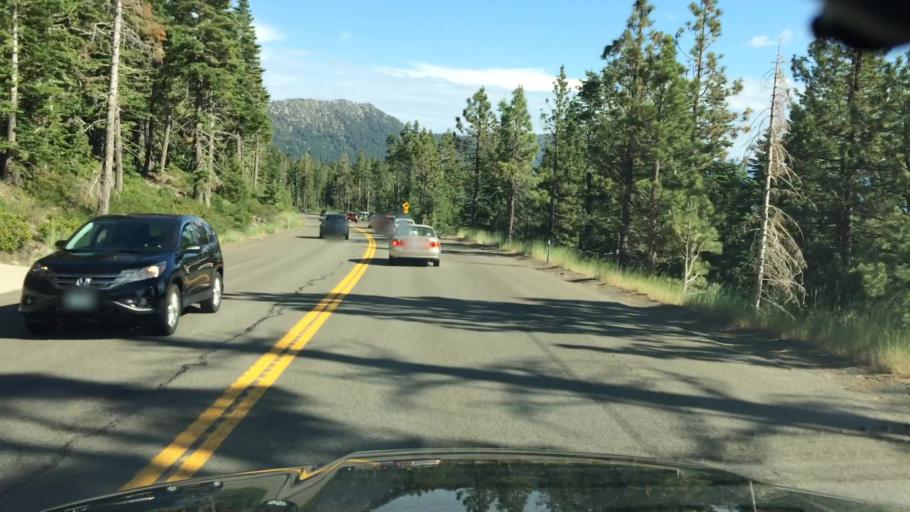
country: US
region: Nevada
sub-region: Washoe County
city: Incline Village
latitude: 39.2705
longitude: -119.9325
